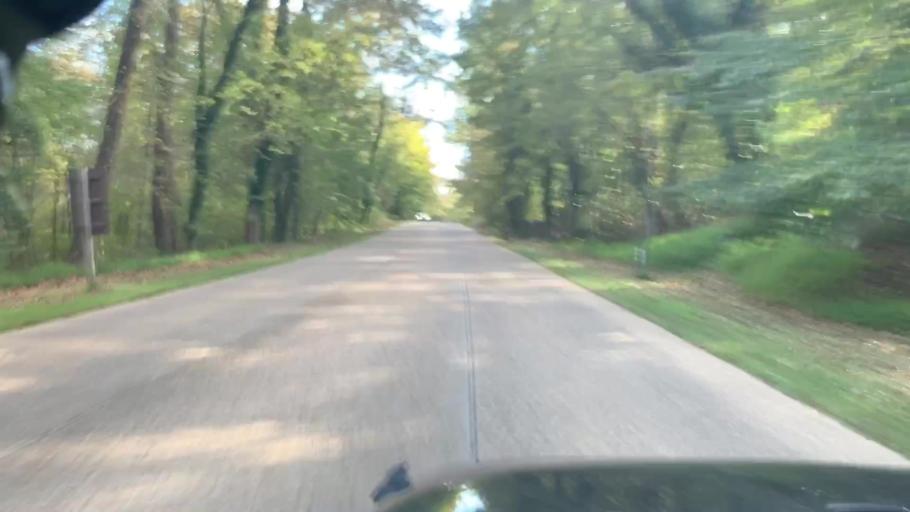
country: US
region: Virginia
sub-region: City of Williamsburg
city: Williamsburg
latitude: 37.2627
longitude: -76.7024
